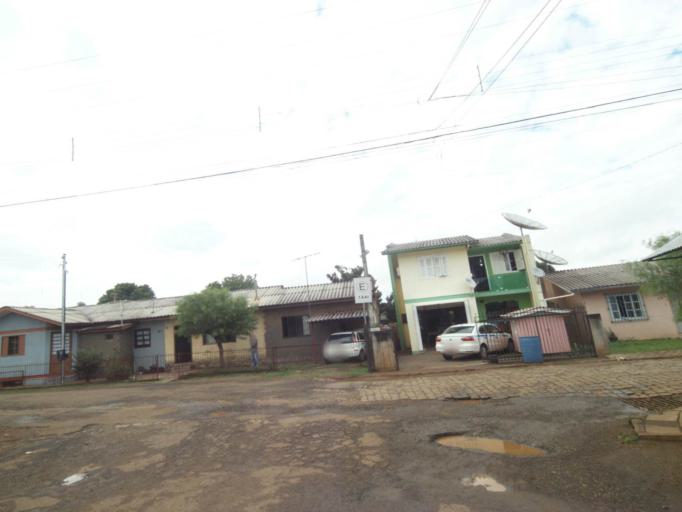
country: BR
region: Rio Grande do Sul
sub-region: Lagoa Vermelha
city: Lagoa Vermelha
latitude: -28.2218
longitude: -51.5224
